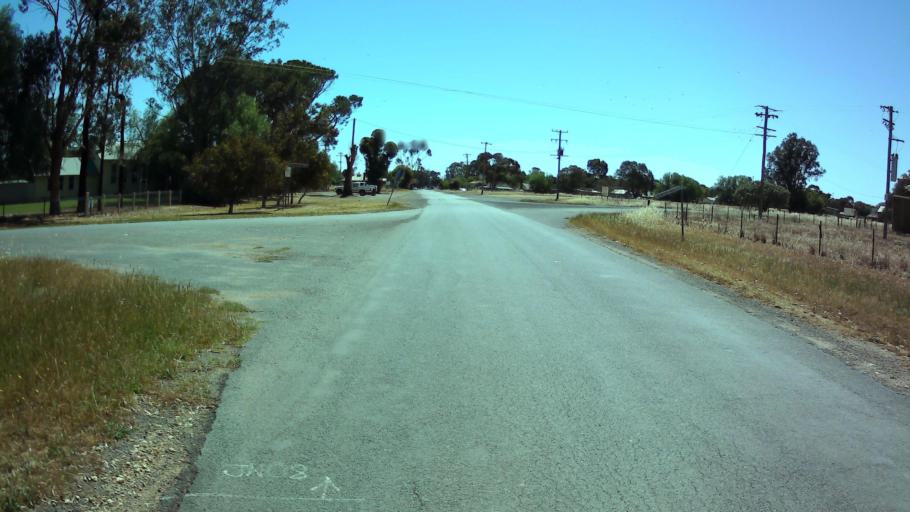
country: AU
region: New South Wales
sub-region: Weddin
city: Grenfell
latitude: -33.9983
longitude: 148.3998
